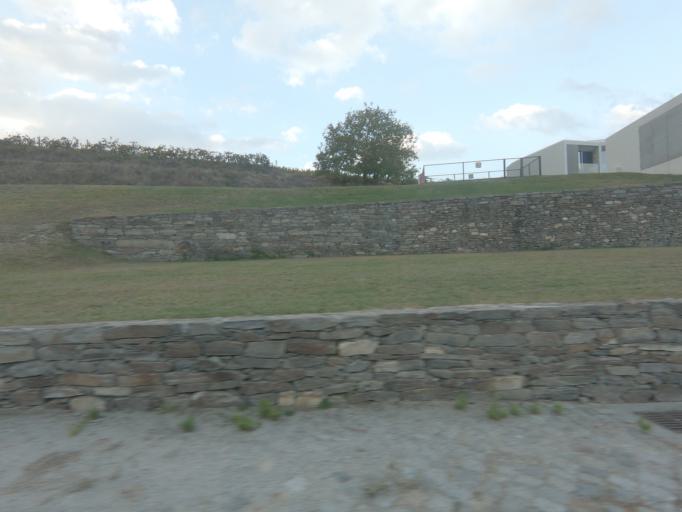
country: PT
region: Vila Real
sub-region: Mesao Frio
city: Mesao Frio
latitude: 41.1670
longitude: -7.8488
